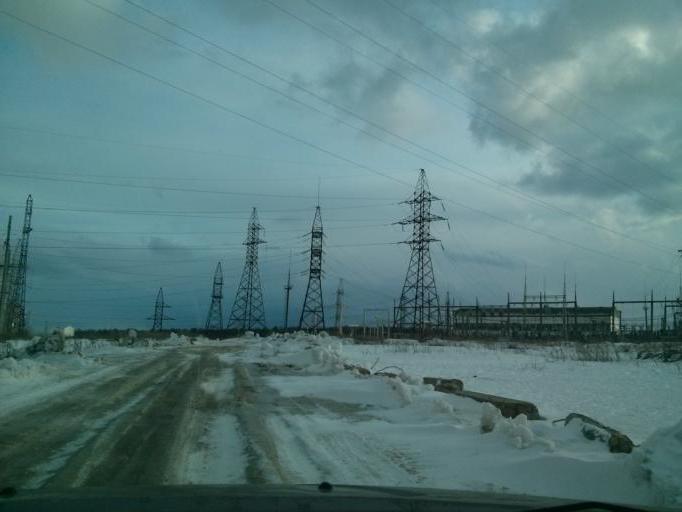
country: RU
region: Nizjnij Novgorod
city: Afonino
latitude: 56.2661
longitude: 44.0308
